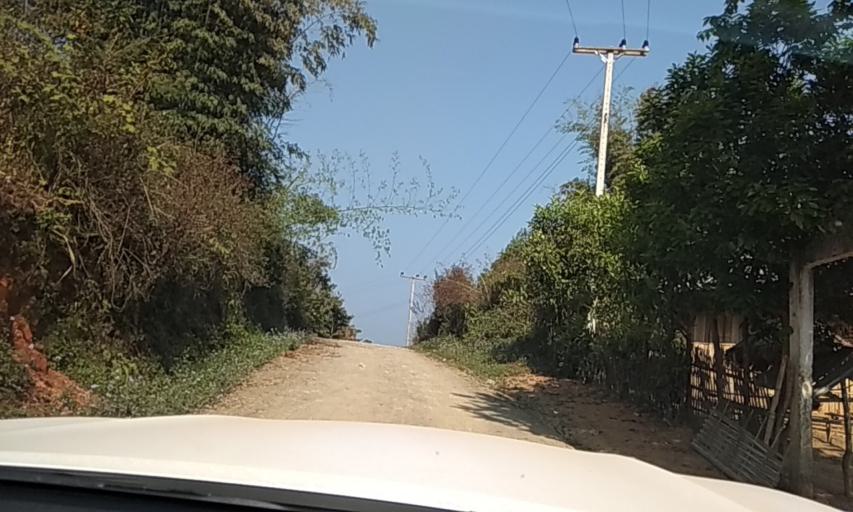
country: LA
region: Phongsali
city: Phongsali
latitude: 21.6981
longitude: 102.0818
